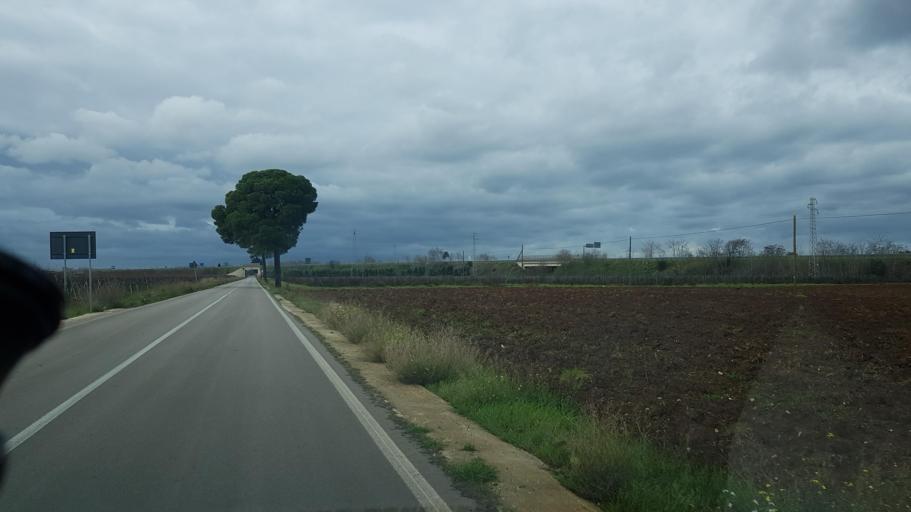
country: IT
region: Apulia
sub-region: Provincia di Brindisi
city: Francavilla Fontana
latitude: 40.5447
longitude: 17.5550
